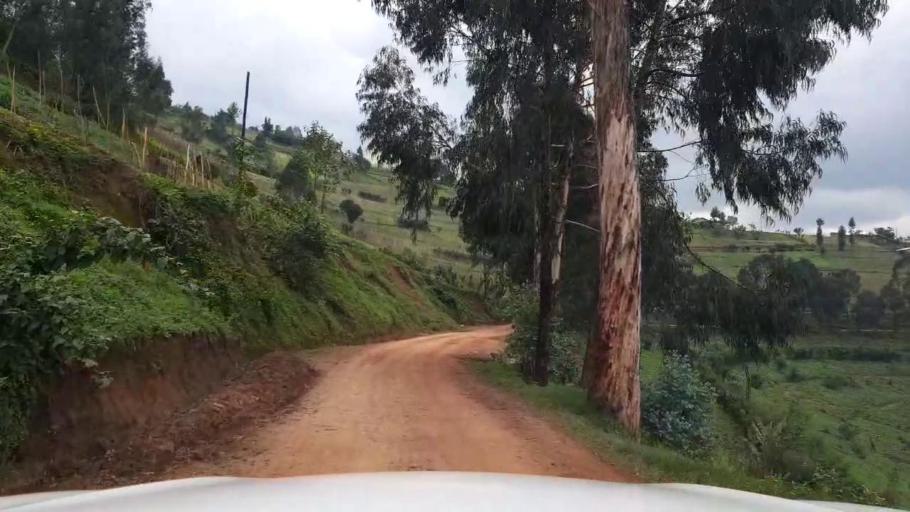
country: UG
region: Western Region
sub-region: Kabale District
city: Kabale
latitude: -1.4279
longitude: 29.8674
